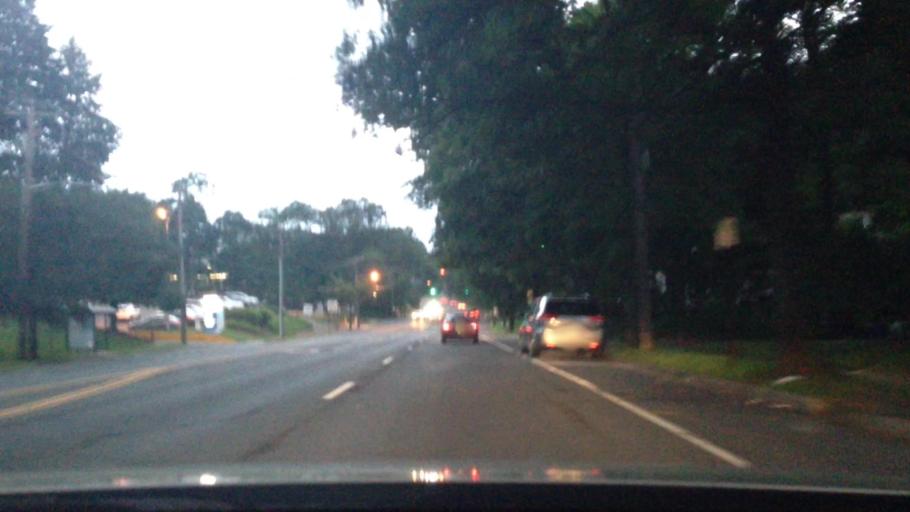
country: US
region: New York
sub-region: Nassau County
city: Lake Success
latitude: 40.7749
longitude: -73.7032
